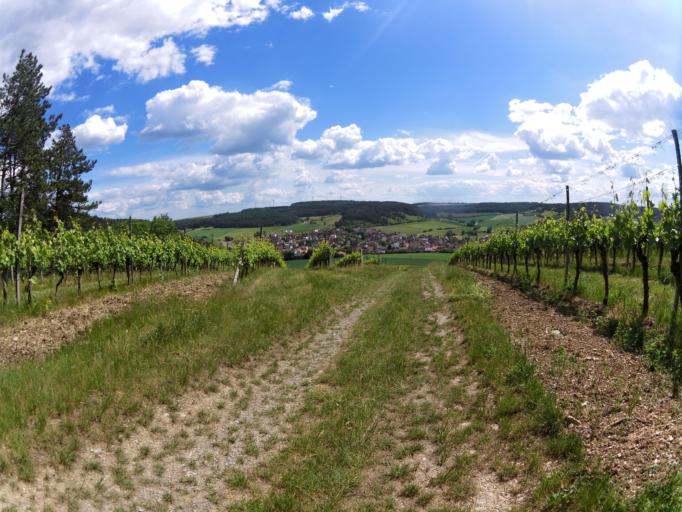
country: DE
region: Bavaria
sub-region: Regierungsbezirk Unterfranken
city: Erlabrunn
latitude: 49.8648
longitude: 9.8120
